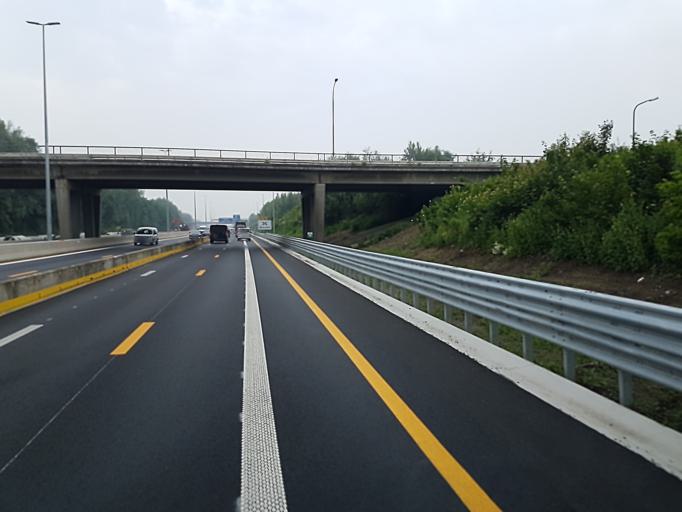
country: BE
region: Flanders
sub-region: Provincie West-Vlaanderen
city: Wevelgem
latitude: 50.8201
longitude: 3.1976
